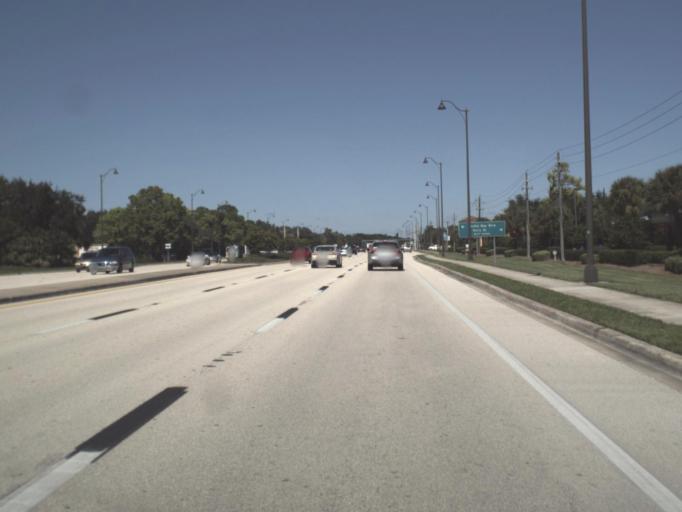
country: US
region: Florida
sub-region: Lee County
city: Bonita Springs
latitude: 26.3438
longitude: -81.8070
